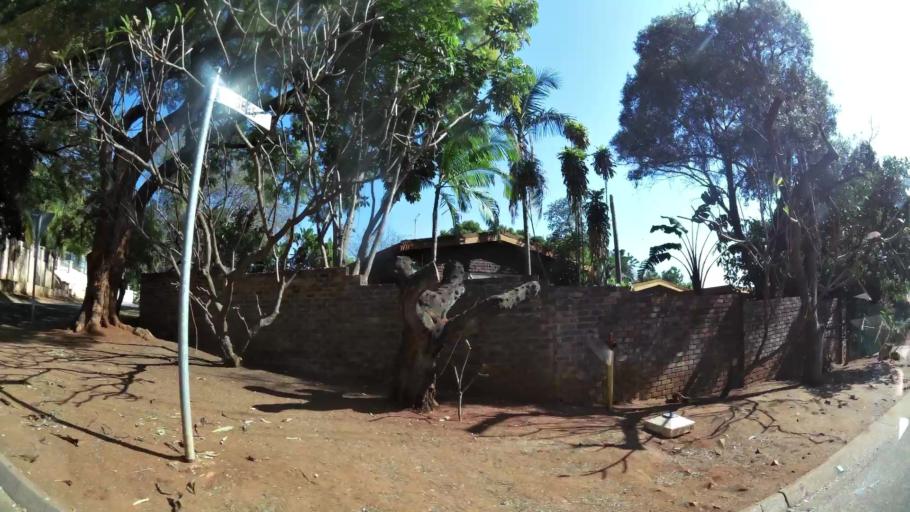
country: ZA
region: Gauteng
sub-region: City of Tshwane Metropolitan Municipality
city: Pretoria
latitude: -25.6891
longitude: 28.2252
